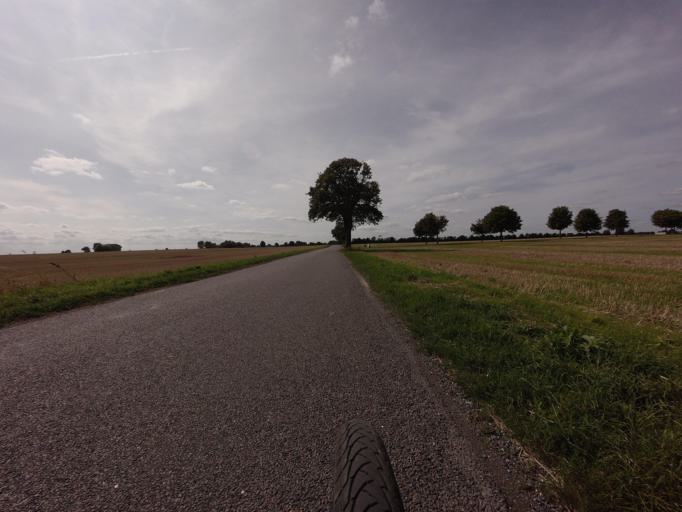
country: DK
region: Zealand
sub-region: Stevns Kommune
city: Store Heddinge
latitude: 55.2438
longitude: 12.3131
